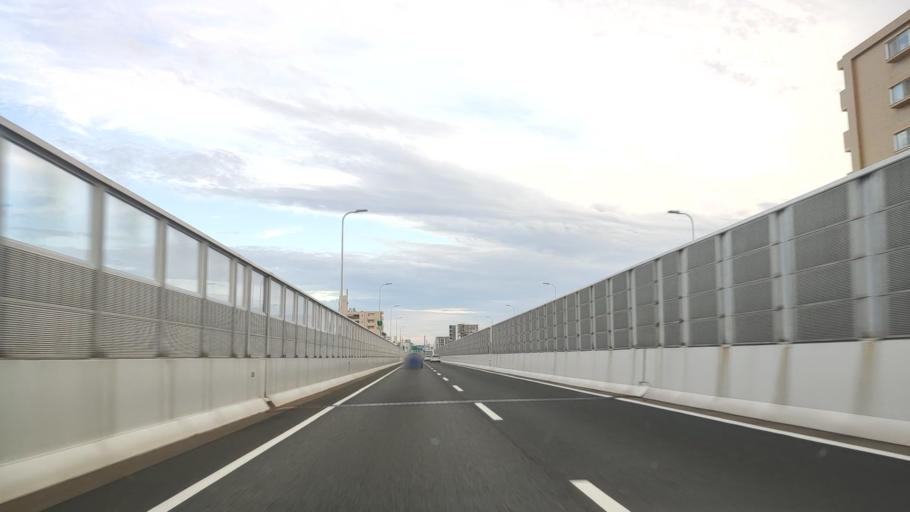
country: JP
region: Aichi
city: Nagoya-shi
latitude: 35.2075
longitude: 136.9113
